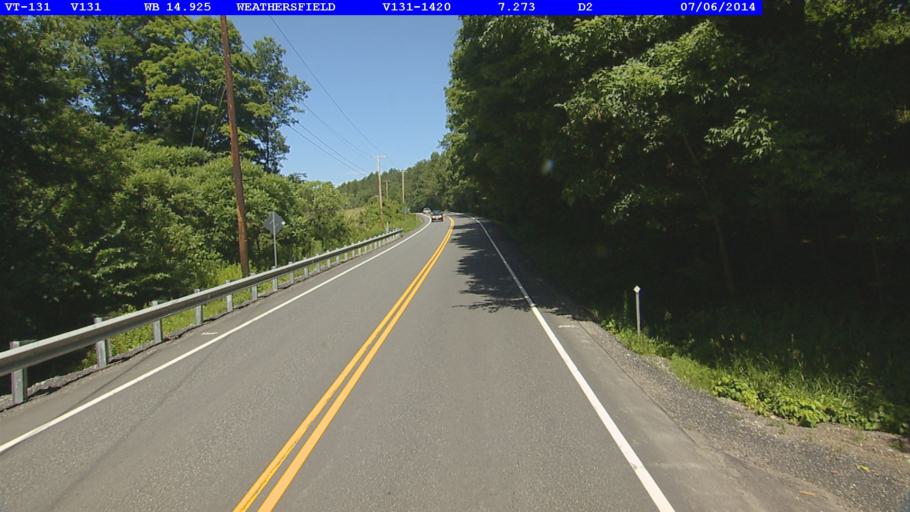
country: US
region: New Hampshire
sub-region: Sullivan County
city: Claremont
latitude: 43.4045
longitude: -72.4311
